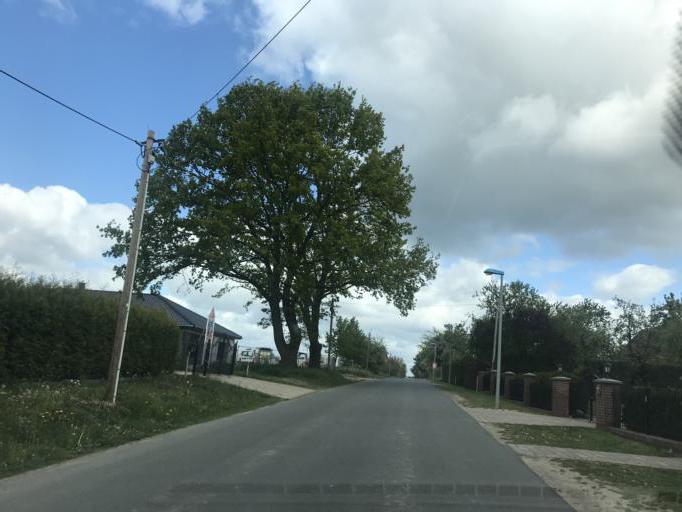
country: DE
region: Brandenburg
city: Gransee
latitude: 52.9241
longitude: 13.1827
